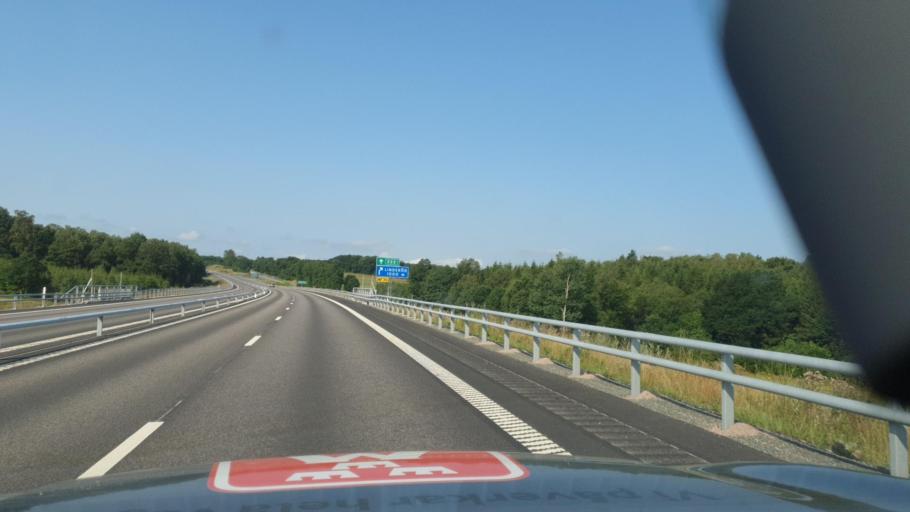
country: SE
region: Skane
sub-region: Hassleholms Kommun
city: Vinslov
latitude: 55.9449
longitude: 13.8713
